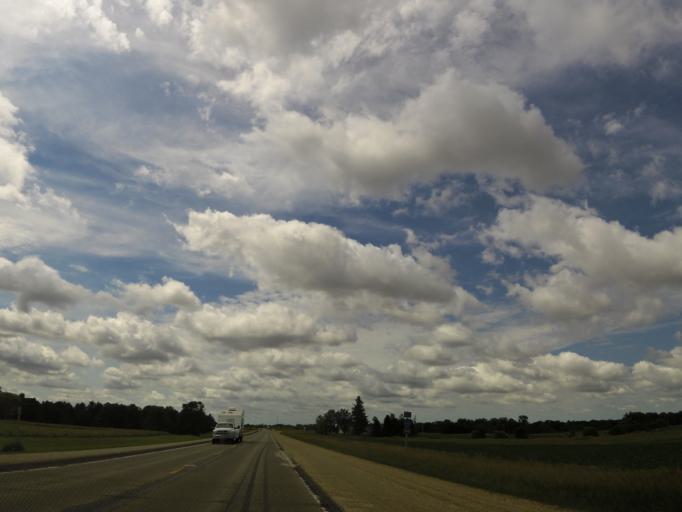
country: US
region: Iowa
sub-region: Chickasaw County
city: New Hampton
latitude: 43.2524
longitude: -92.2981
